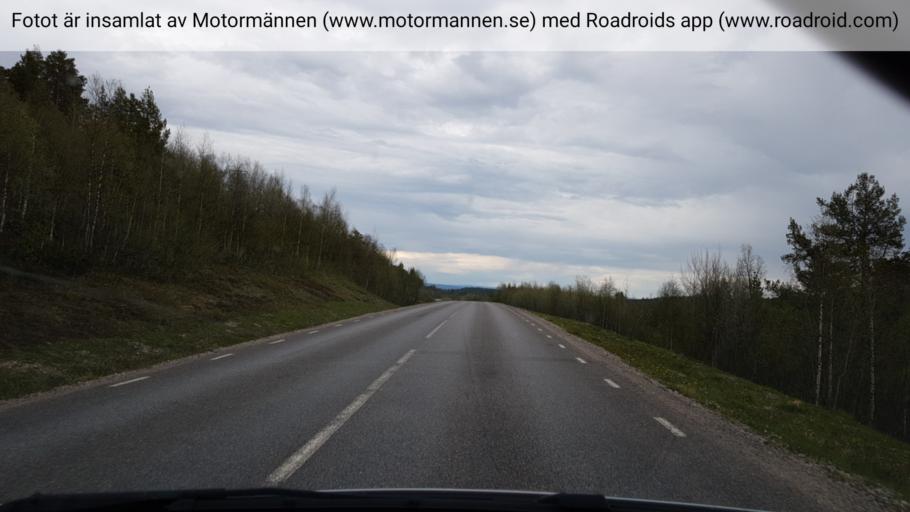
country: SE
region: Norrbotten
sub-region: Arjeplogs Kommun
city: Arjeplog
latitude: 66.4445
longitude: 16.8045
